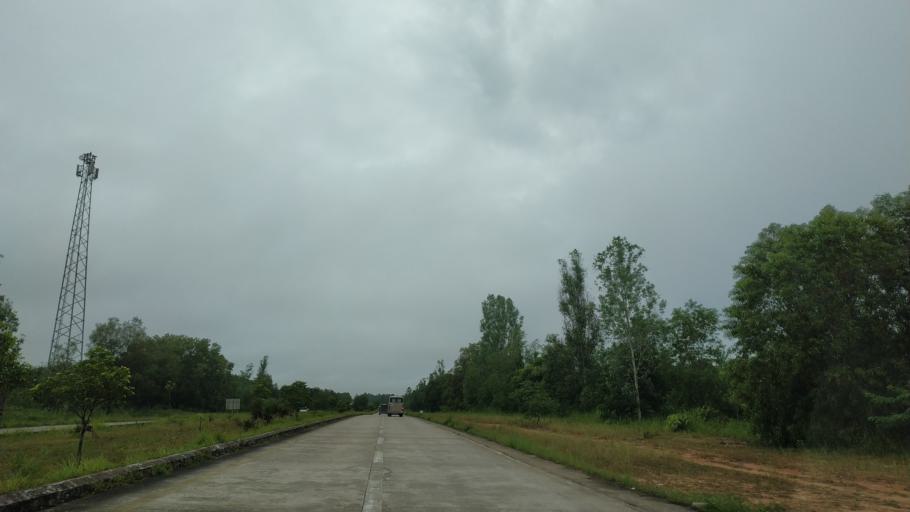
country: MM
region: Bago
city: Bago
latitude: 17.3891
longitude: 96.3156
